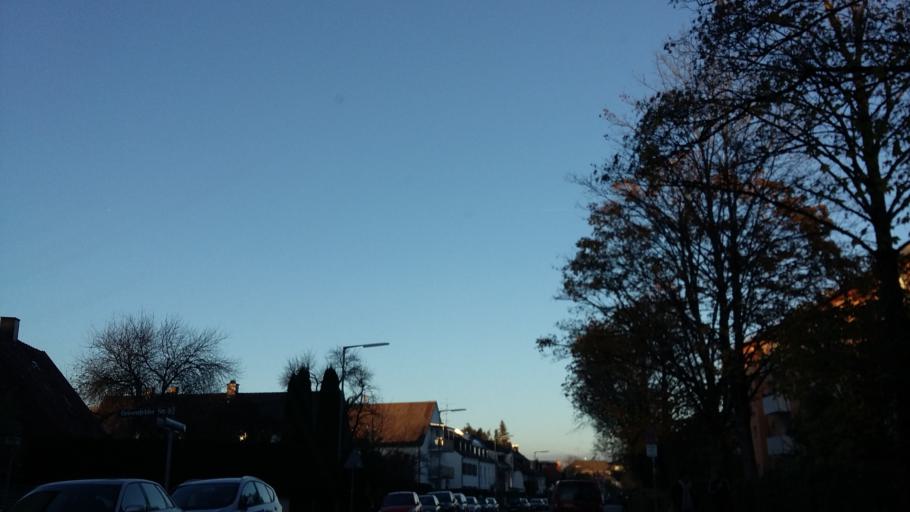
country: DE
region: Bavaria
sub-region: Upper Bavaria
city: Pasing
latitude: 48.1297
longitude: 11.4954
